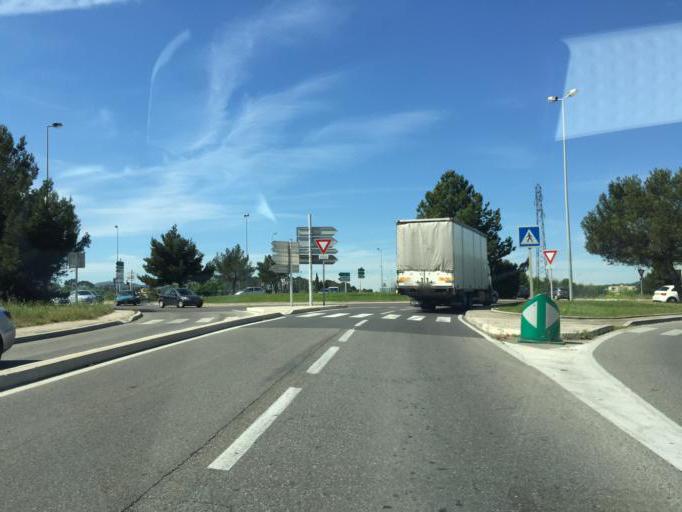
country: FR
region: Provence-Alpes-Cote d'Azur
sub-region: Departement des Bouches-du-Rhone
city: Aubagne
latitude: 43.2983
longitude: 5.5915
